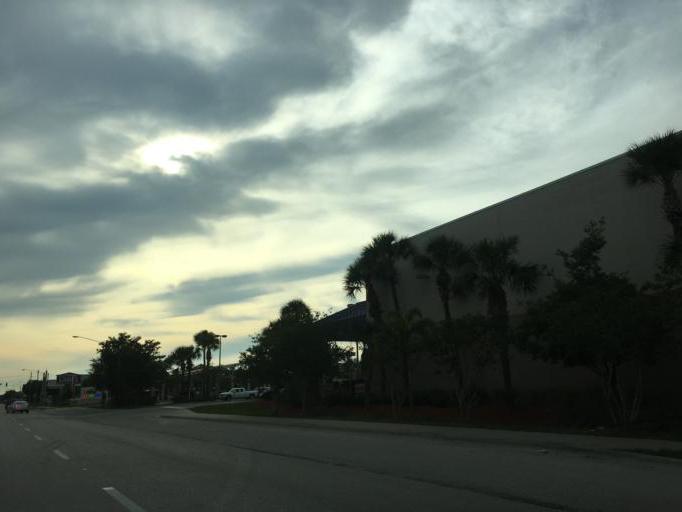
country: US
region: Florida
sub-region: Pinellas County
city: Saint Petersburg
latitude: 27.7920
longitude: -82.6654
